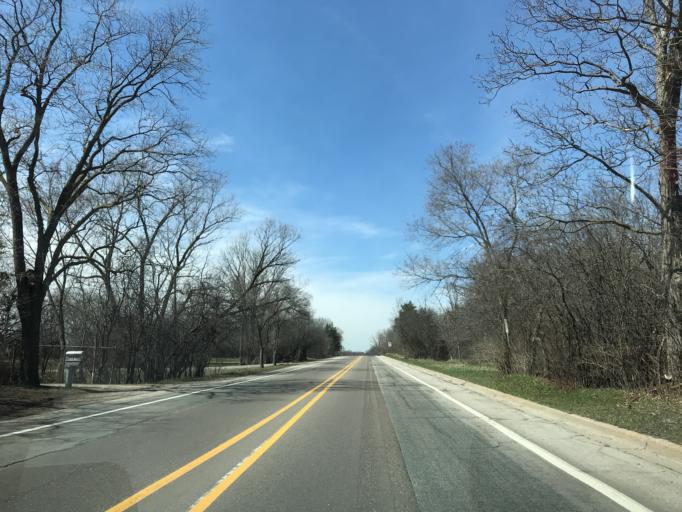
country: US
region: Michigan
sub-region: Washtenaw County
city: Ann Arbor
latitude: 42.2570
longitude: -83.7515
